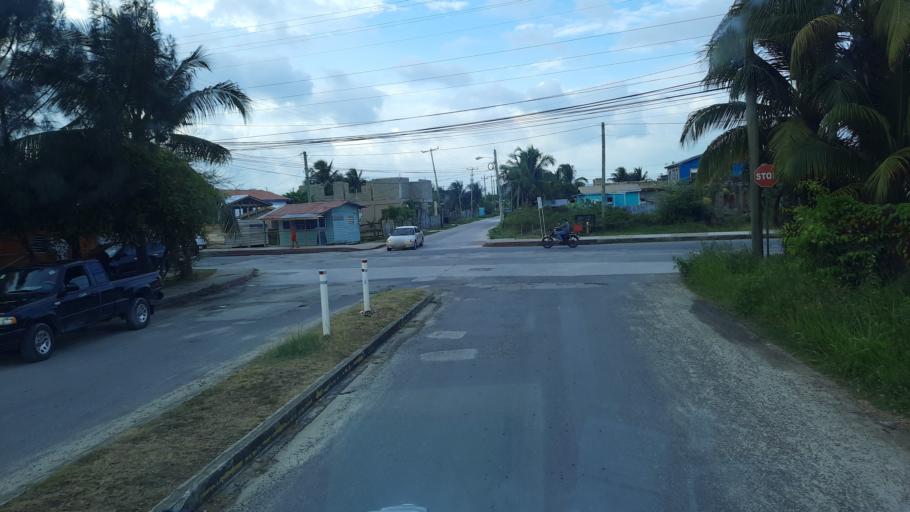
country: BZ
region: Belize
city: Belize City
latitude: 17.5016
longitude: -88.2061
